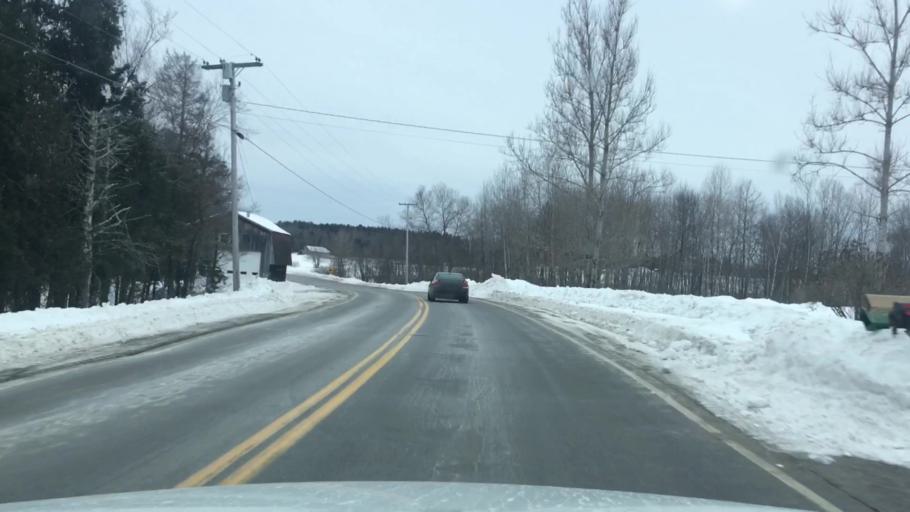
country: US
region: Maine
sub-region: Penobscot County
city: Garland
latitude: 44.9917
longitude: -69.0866
